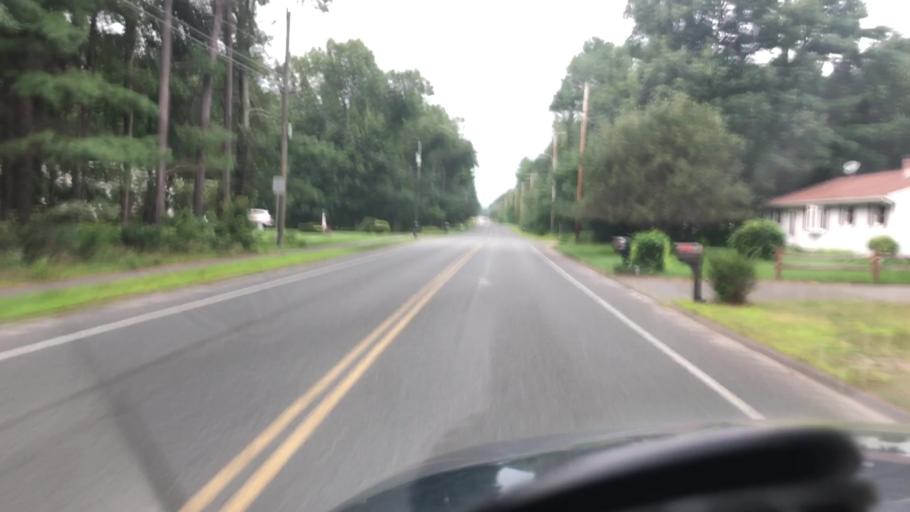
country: US
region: Massachusetts
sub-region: Hampshire County
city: Southampton
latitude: 42.1963
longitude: -72.6875
